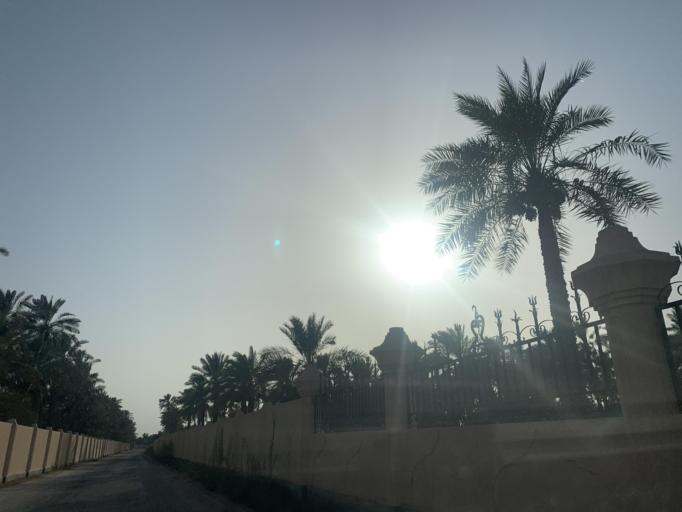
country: BH
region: Central Governorate
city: Madinat Hamad
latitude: 26.1846
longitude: 50.4654
